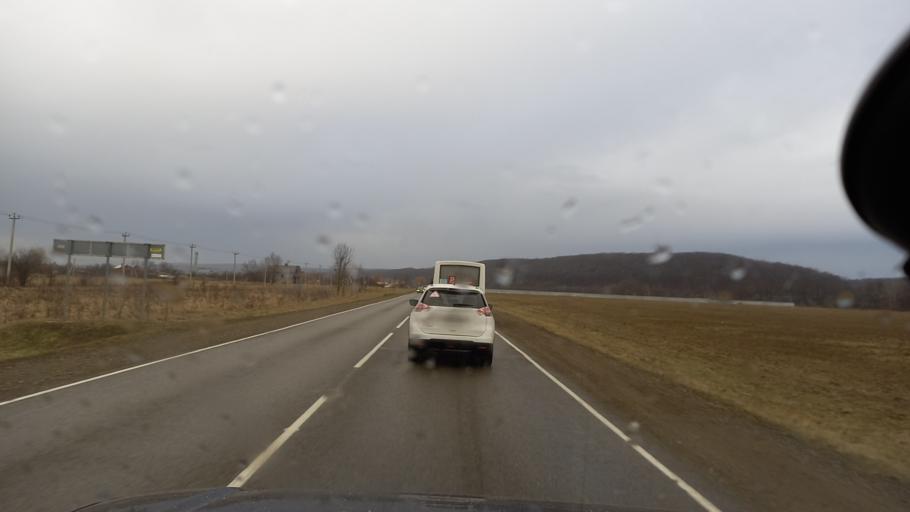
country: RU
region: Adygeya
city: Tul'skiy
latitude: 44.5313
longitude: 40.1378
